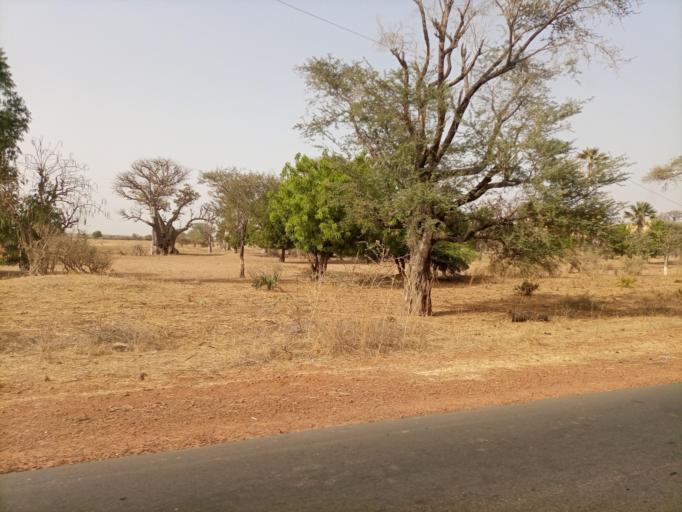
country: SN
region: Fatick
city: Foundiougne
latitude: 14.1184
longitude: -16.4487
